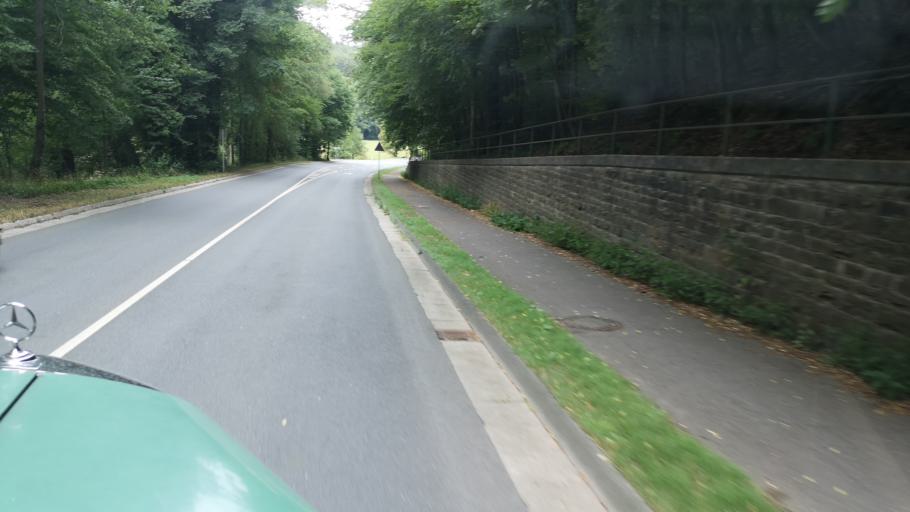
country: DE
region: North Rhine-Westphalia
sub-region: Regierungsbezirk Koln
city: Odenthal
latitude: 51.0560
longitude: 7.1354
